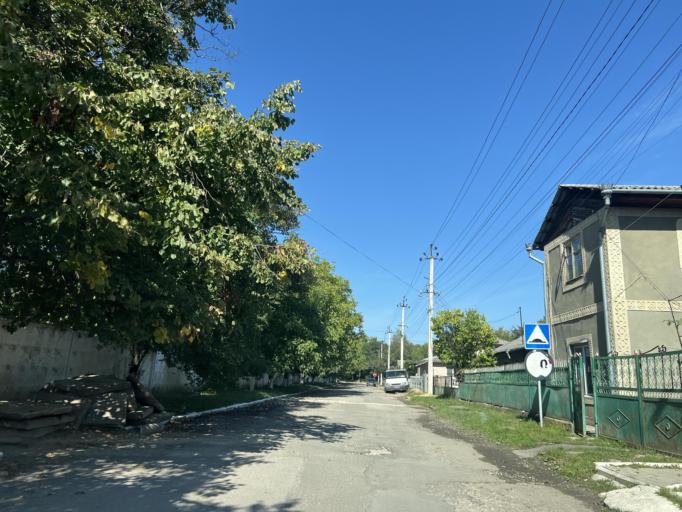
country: RO
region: Iasi
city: Ungheni-Prut
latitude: 47.1979
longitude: 27.7932
